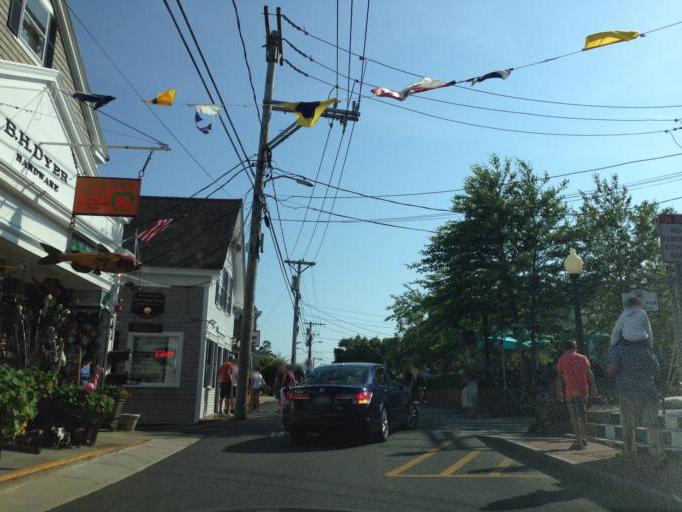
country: US
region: Massachusetts
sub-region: Barnstable County
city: Provincetown
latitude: 42.0480
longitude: -70.1897
